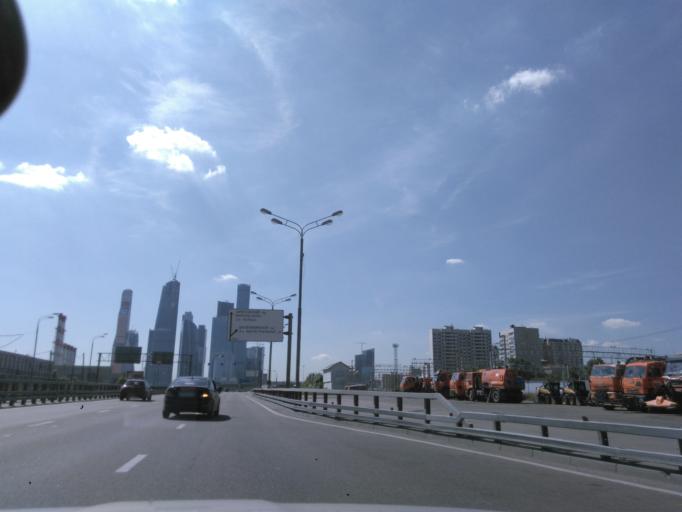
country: RU
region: Moskovskaya
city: Presnenskiy
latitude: 55.7639
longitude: 37.5207
